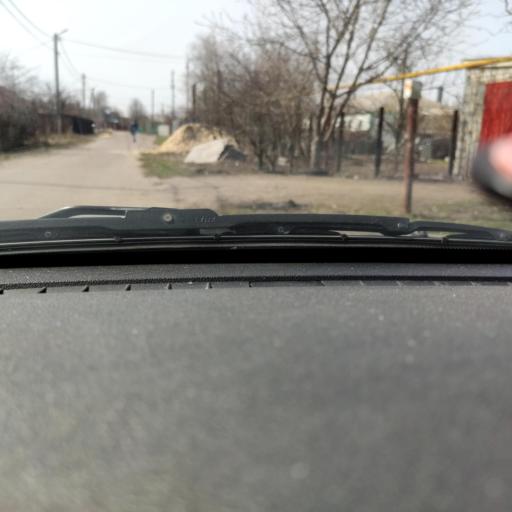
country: RU
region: Voronezj
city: Novaya Usman'
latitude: 51.6294
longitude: 39.4060
